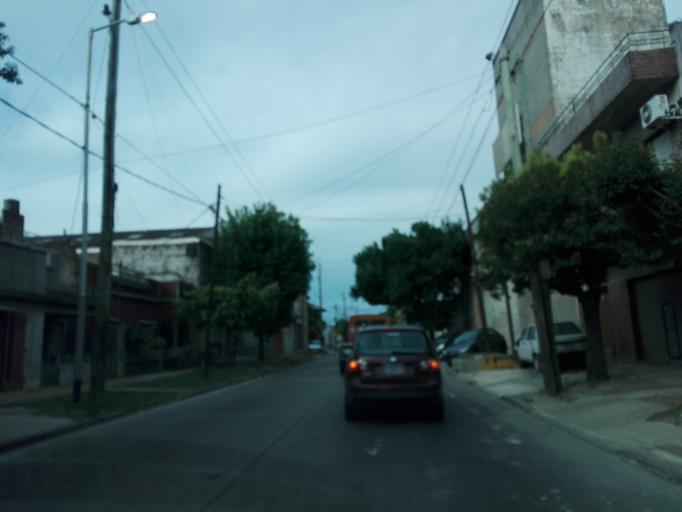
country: AR
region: Buenos Aires
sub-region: Partido de Avellaneda
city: Avellaneda
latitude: -34.6872
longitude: -58.3495
